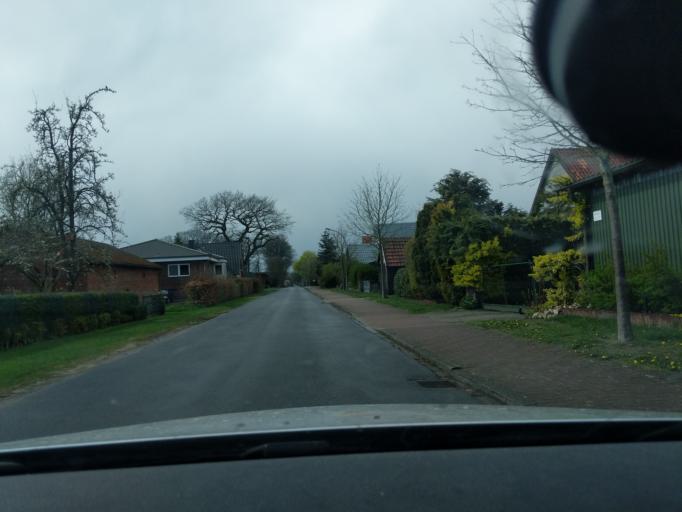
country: DE
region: Lower Saxony
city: Ahlerstedt
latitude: 53.4090
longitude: 9.4617
